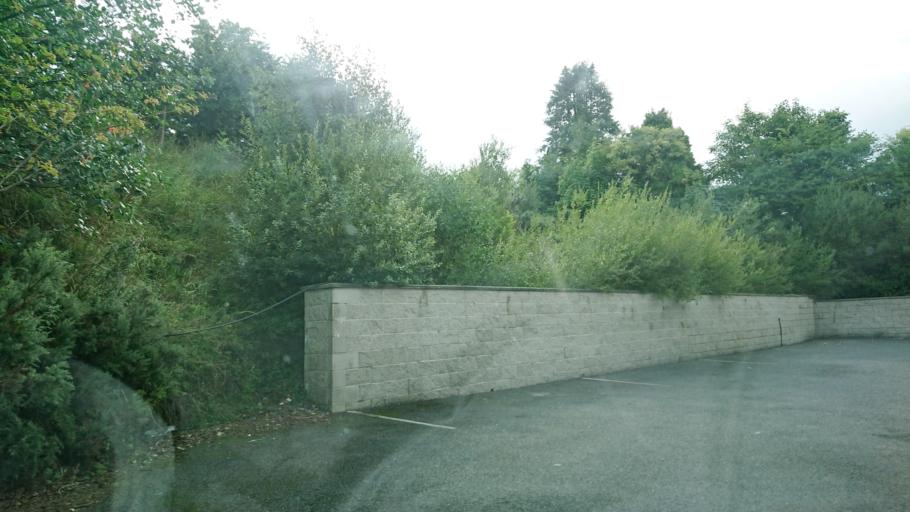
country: IE
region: Munster
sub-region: County Cork
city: Millstreet
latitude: 52.0834
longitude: -9.2101
